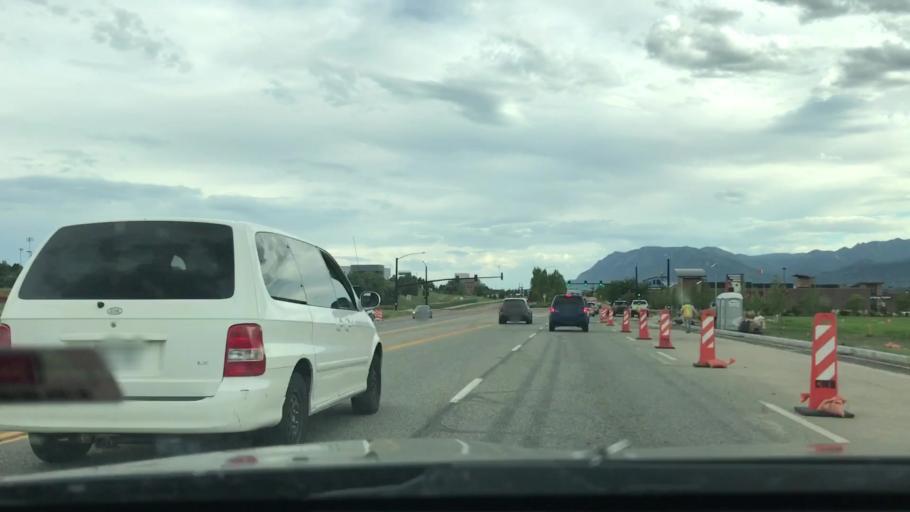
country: US
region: Colorado
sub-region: El Paso County
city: Colorado Springs
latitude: 38.9092
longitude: -104.8164
